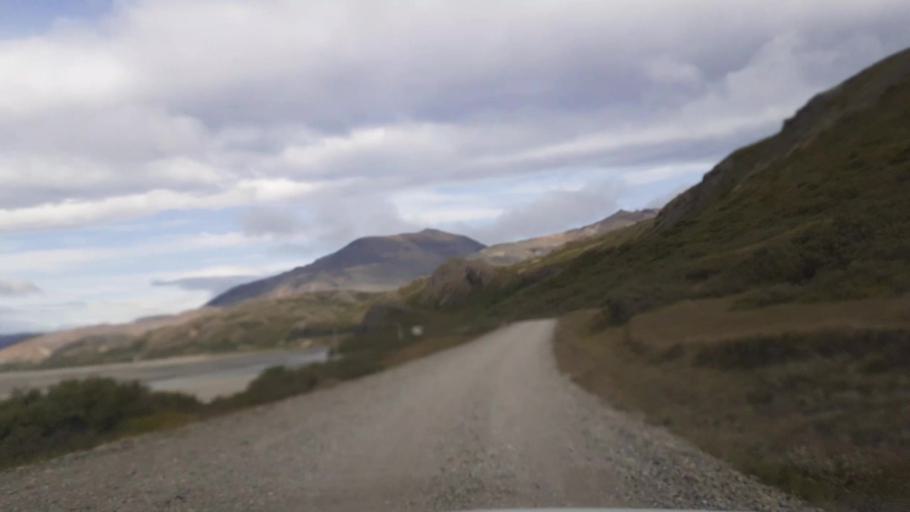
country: IS
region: East
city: Hoefn
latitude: 64.4237
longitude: -14.8808
